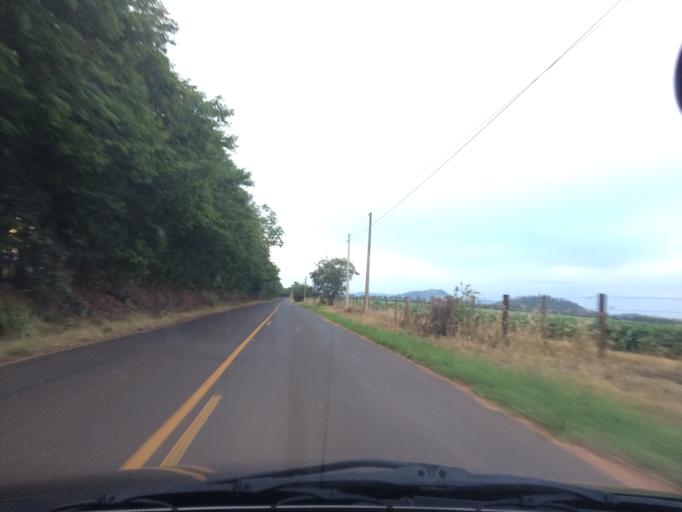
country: BR
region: Sao Paulo
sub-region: Casa Branca
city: Casa Branca
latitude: -21.7401
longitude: -47.1745
